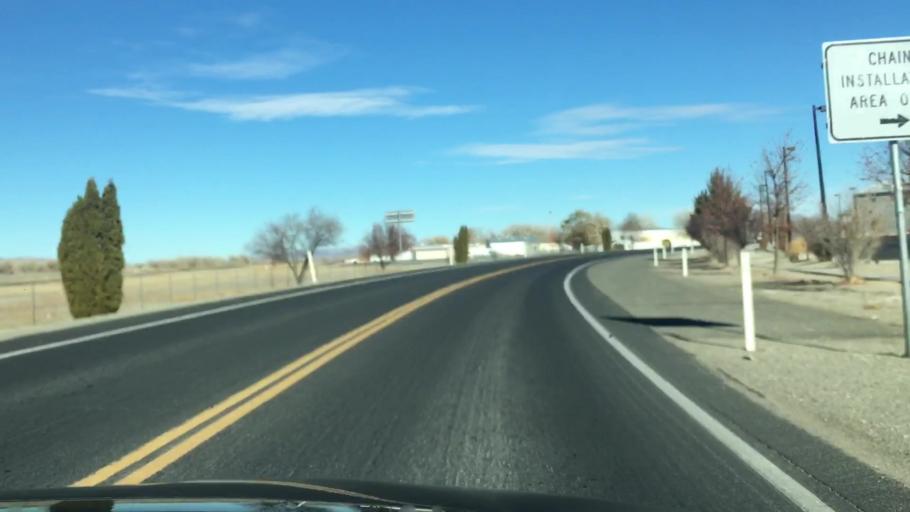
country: US
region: Nevada
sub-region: Lyon County
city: Yerington
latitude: 38.9960
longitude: -119.1622
